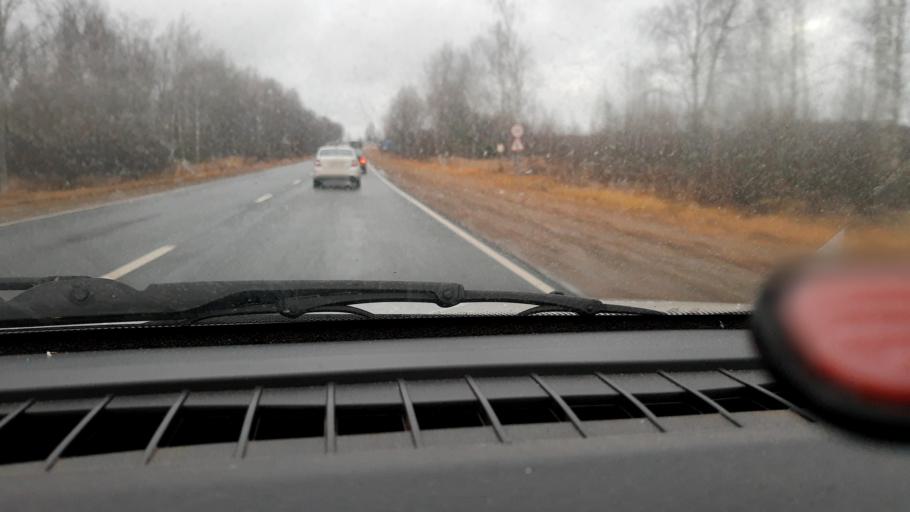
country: RU
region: Nizjnij Novgorod
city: Krasnyye Baki
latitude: 57.0907
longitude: 45.1486
